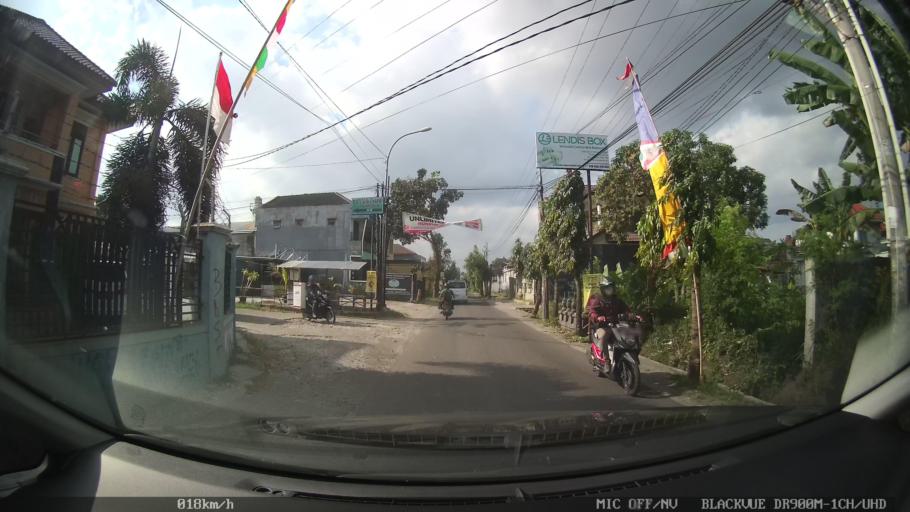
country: ID
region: Daerah Istimewa Yogyakarta
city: Gamping Lor
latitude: -7.7967
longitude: 110.3456
